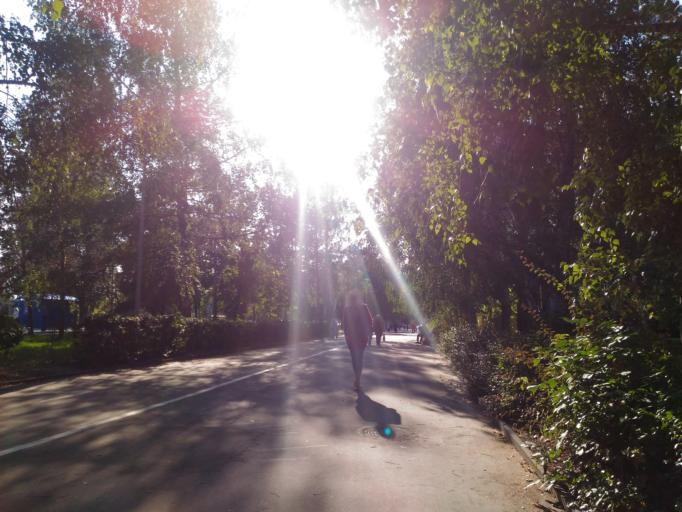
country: RU
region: Ulyanovsk
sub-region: Ulyanovskiy Rayon
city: Ulyanovsk
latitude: 54.3533
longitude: 48.5339
